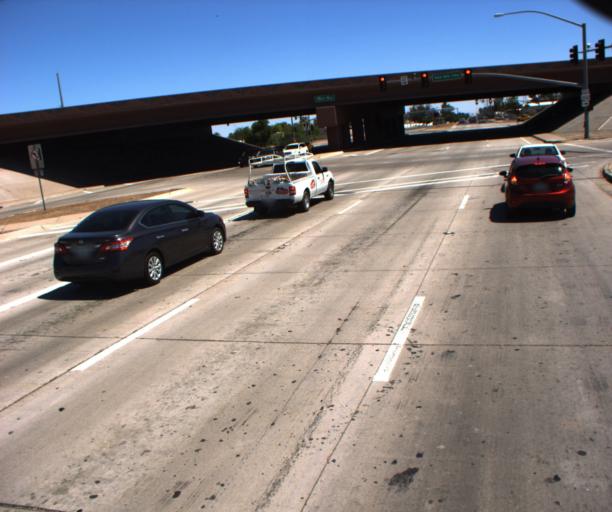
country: US
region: Arizona
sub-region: Maricopa County
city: Mesa
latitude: 33.4561
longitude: -111.8398
